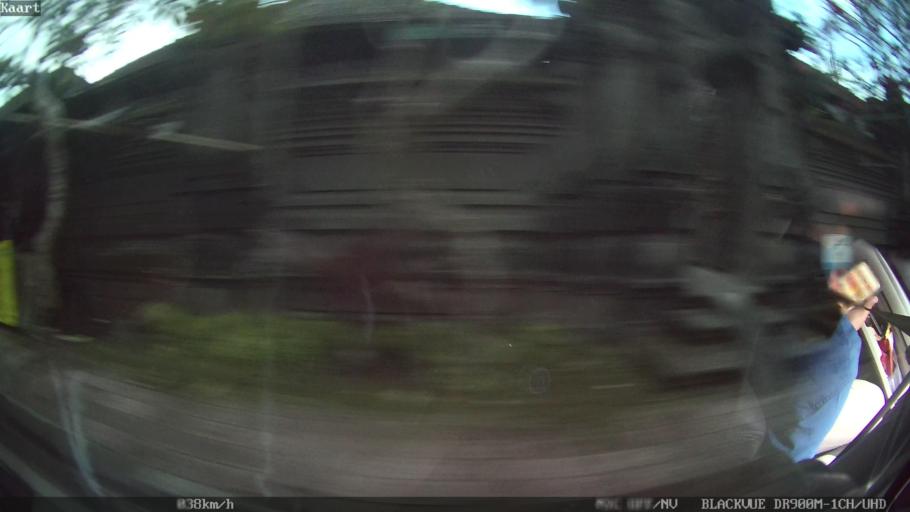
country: ID
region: Bali
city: Bunutan
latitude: -8.4736
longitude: 115.2497
